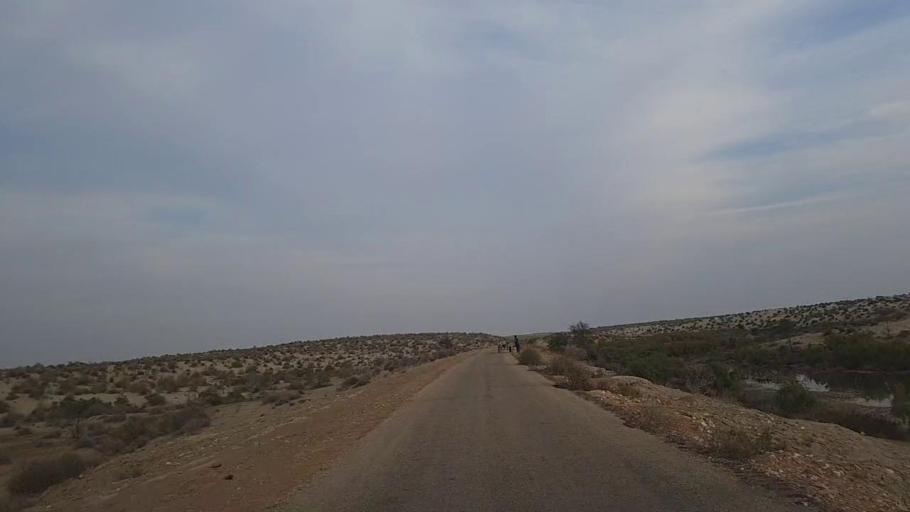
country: PK
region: Sindh
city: Jam Sahib
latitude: 26.4938
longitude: 68.5357
